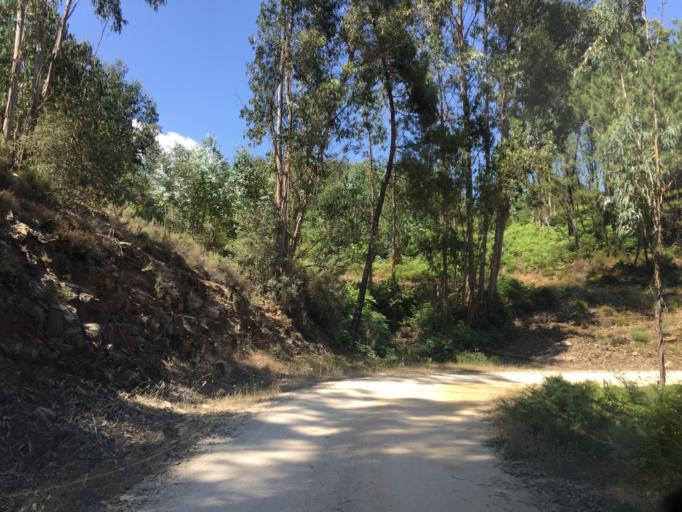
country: PT
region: Leiria
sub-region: Pedrogao Grande
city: Pedrogao Grande
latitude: 39.9289
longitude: -8.1305
